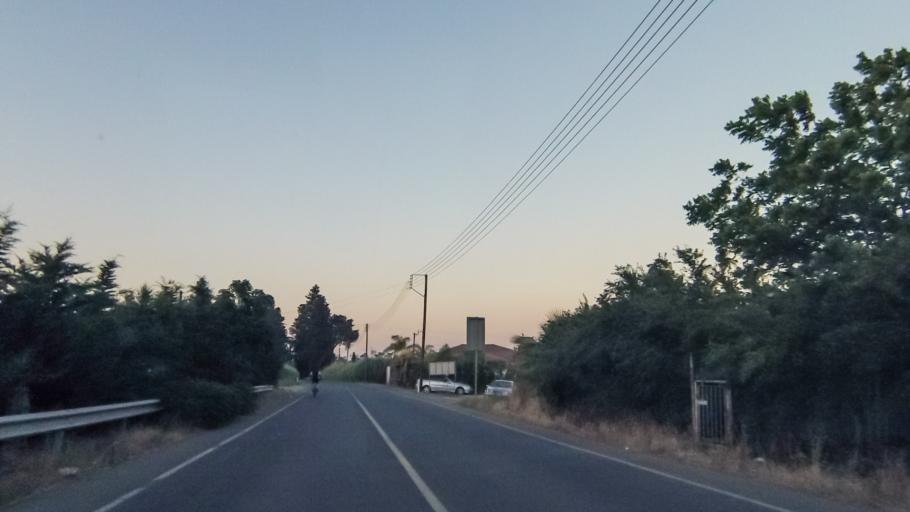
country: CY
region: Limassol
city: Ypsonas
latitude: 34.6524
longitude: 32.9886
